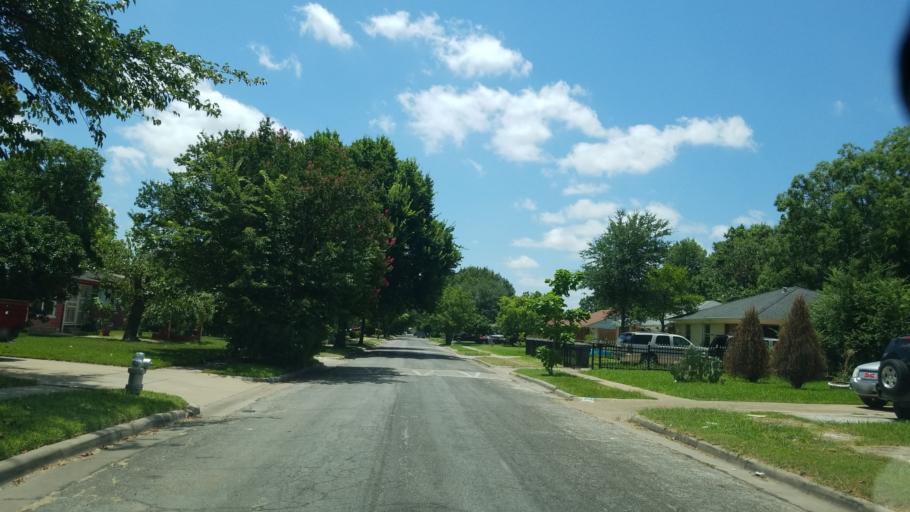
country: US
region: Texas
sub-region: Dallas County
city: Balch Springs
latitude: 32.7468
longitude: -96.6963
